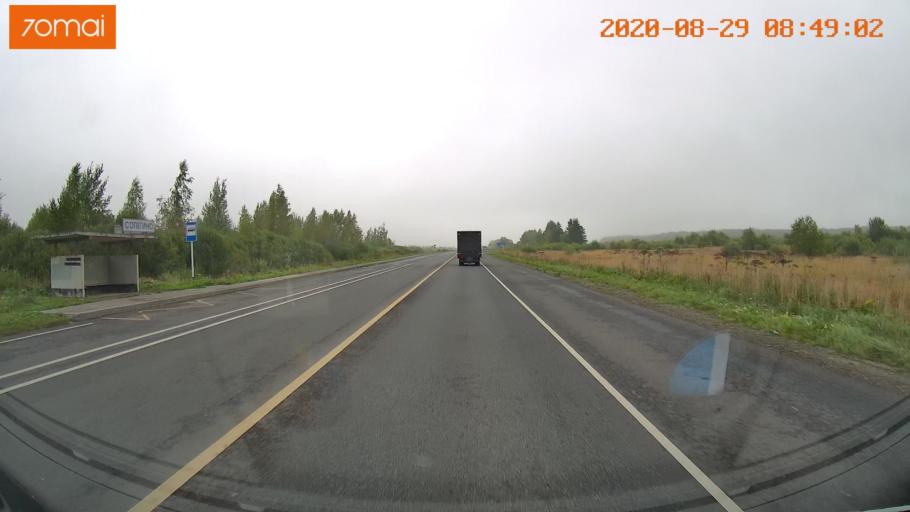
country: RU
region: Ivanovo
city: Vichuga
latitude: 57.1676
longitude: 41.8597
